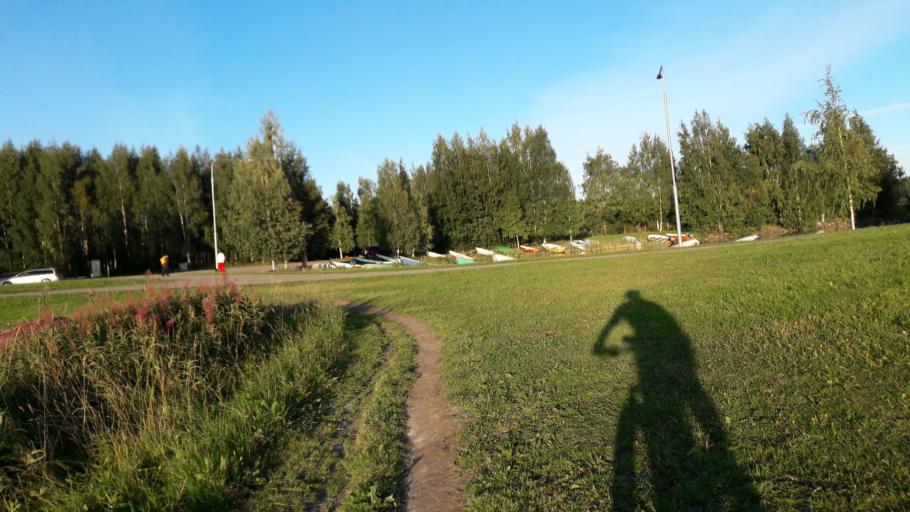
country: FI
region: North Karelia
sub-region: Joensuu
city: Joensuu
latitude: 62.6124
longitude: 29.7072
